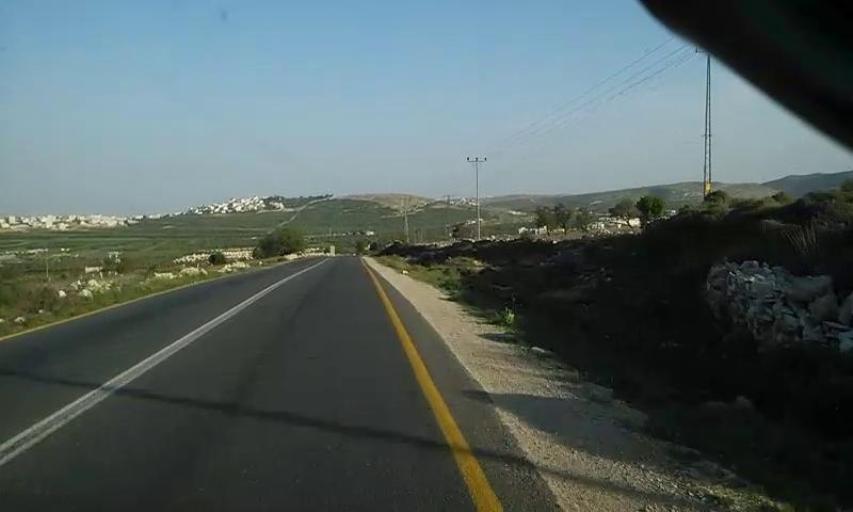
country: PS
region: West Bank
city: Marah Rabbah
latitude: 31.6449
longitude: 35.1920
